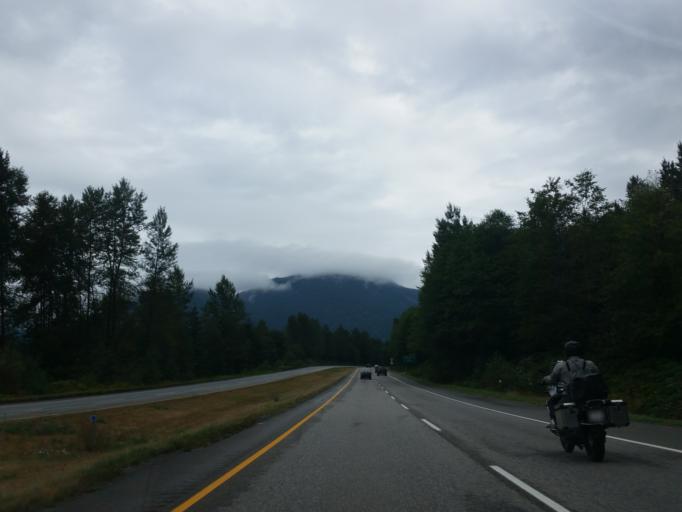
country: CA
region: British Columbia
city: Agassiz
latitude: 49.2775
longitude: -121.6714
